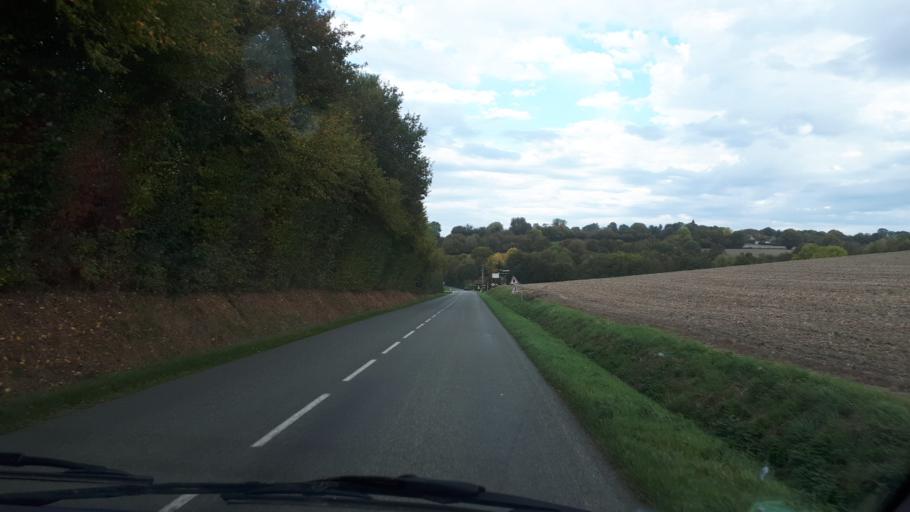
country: FR
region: Centre
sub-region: Departement d'Eure-et-Loir
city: Authon-du-Perche
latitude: 48.2280
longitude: 0.8718
